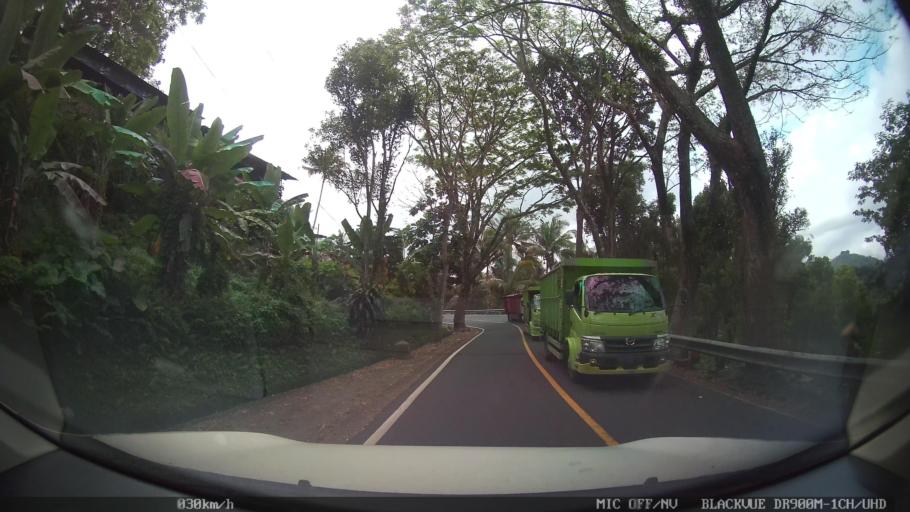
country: ID
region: Bali
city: Banjar Wangsian
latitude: -8.4772
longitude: 115.4016
